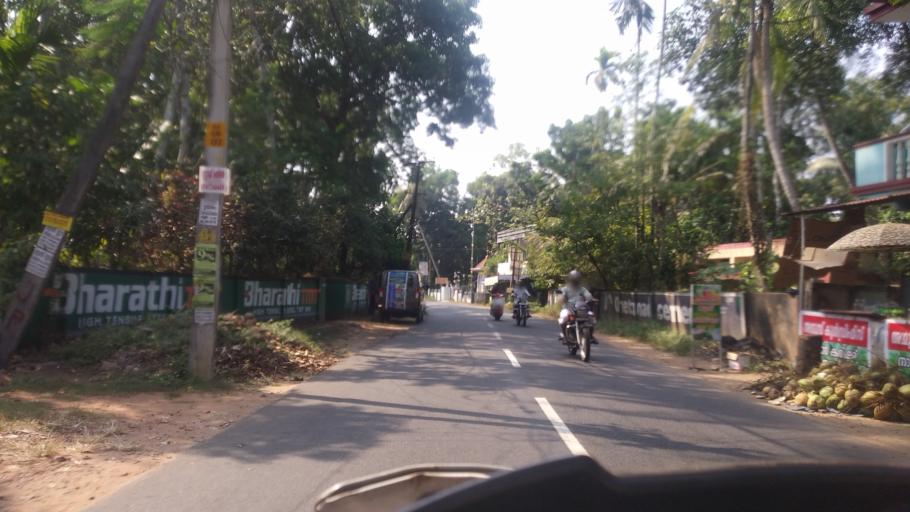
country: IN
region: Kerala
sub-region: Thrissur District
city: Kodungallur
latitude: 10.2066
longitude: 76.1841
